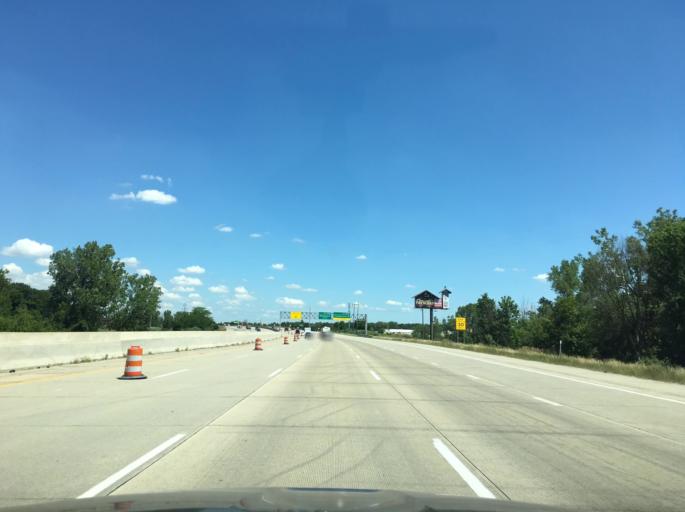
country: US
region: Michigan
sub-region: Saginaw County
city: Bridgeport
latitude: 43.3441
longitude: -83.8635
